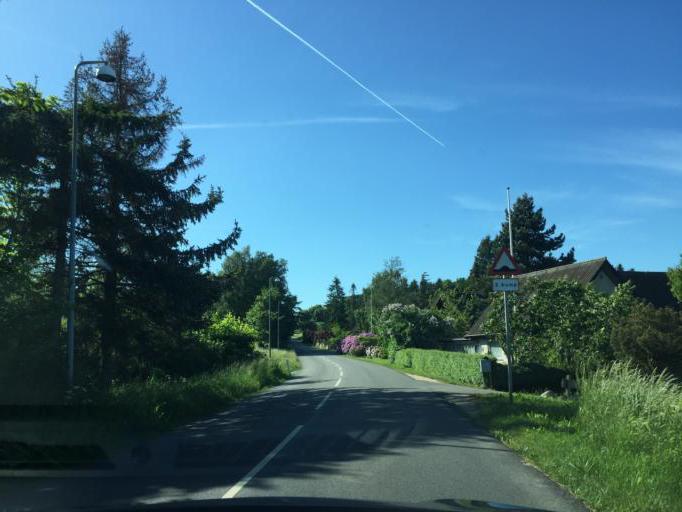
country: DK
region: Zealand
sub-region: Koge Kommune
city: Koge
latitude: 55.4132
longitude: 12.1573
